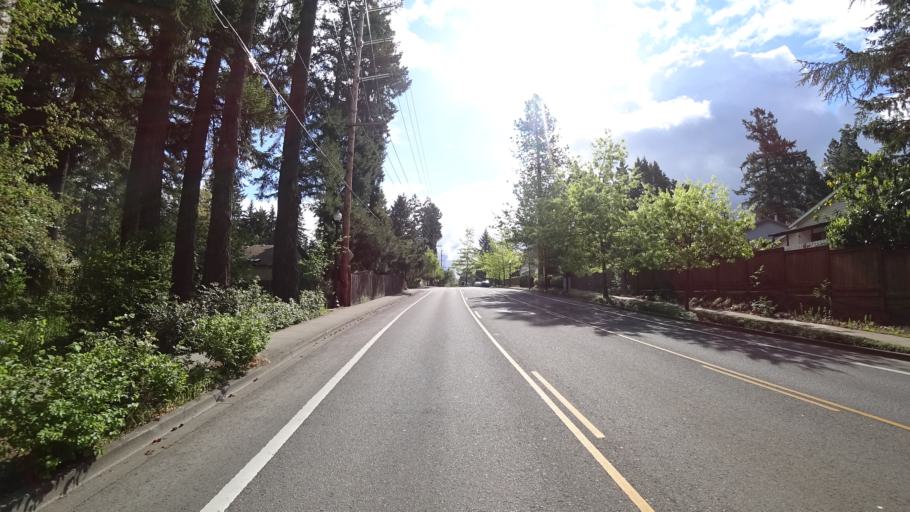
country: US
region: Oregon
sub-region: Washington County
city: Beaverton
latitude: 45.4657
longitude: -122.8300
